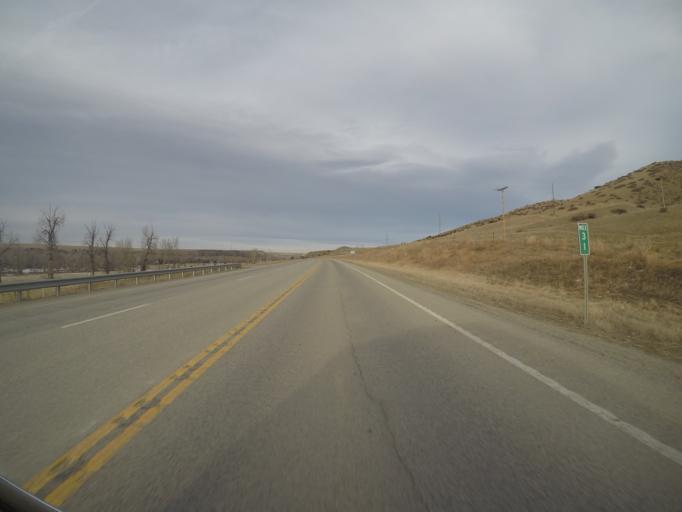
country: US
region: Montana
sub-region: Stillwater County
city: Absarokee
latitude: 45.4960
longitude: -109.4498
